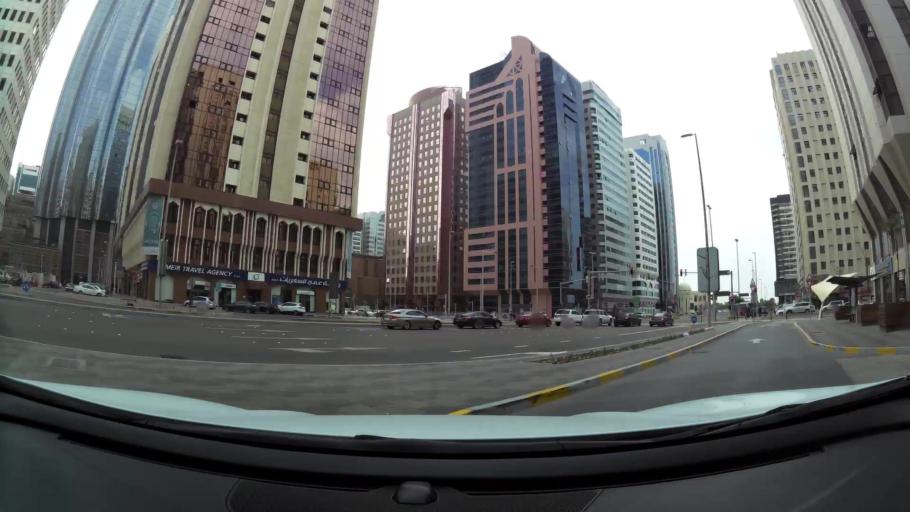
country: AE
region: Abu Dhabi
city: Abu Dhabi
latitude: 24.4894
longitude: 54.3585
